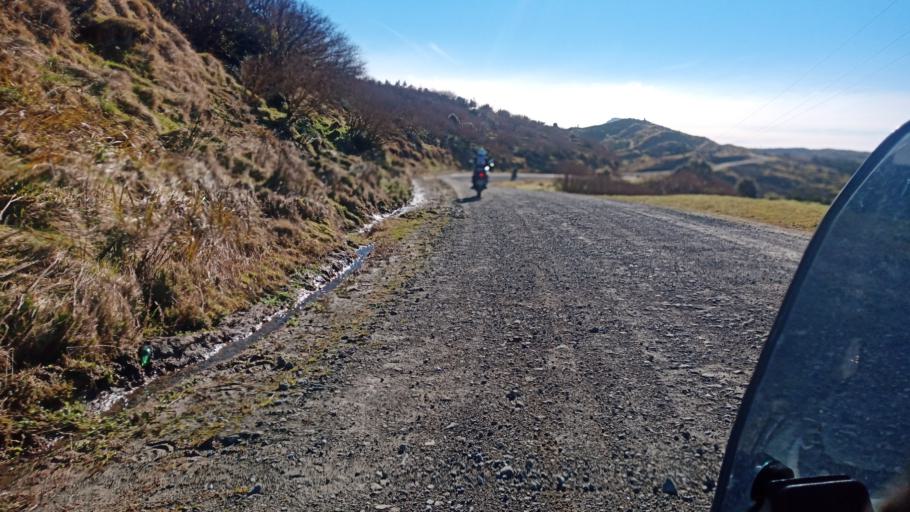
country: NZ
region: Gisborne
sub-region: Gisborne District
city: Gisborne
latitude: -38.1841
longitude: 177.8215
